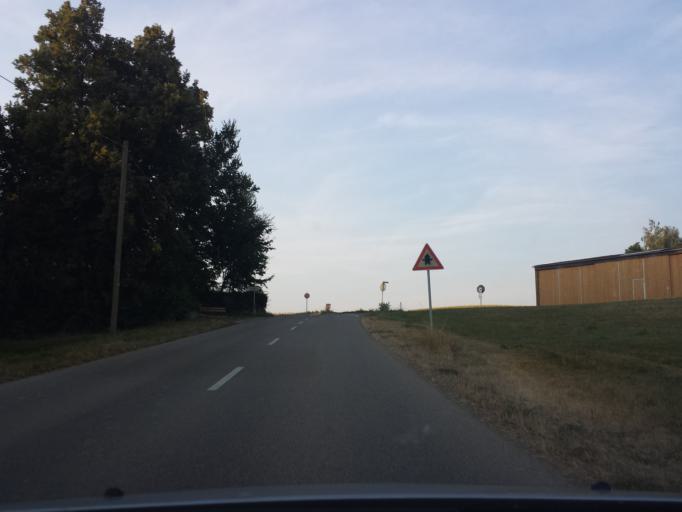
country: DE
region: Bavaria
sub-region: Swabia
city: Guenzburg
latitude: 48.4385
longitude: 10.2991
